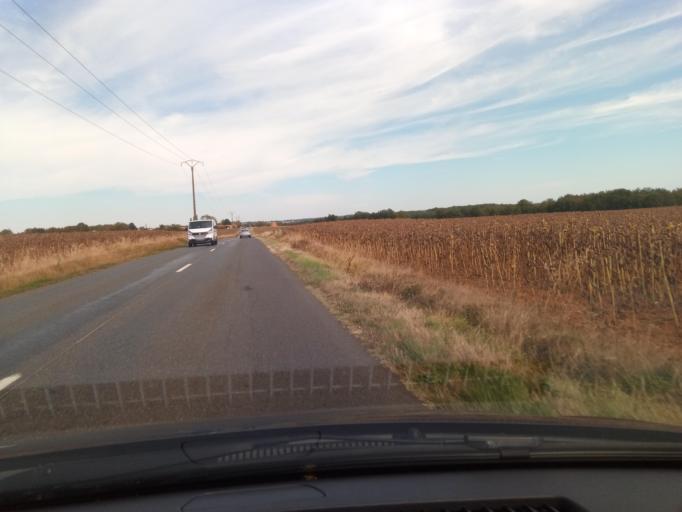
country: FR
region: Poitou-Charentes
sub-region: Departement de la Vienne
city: Chauvigny
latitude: 46.5531
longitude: 0.6075
